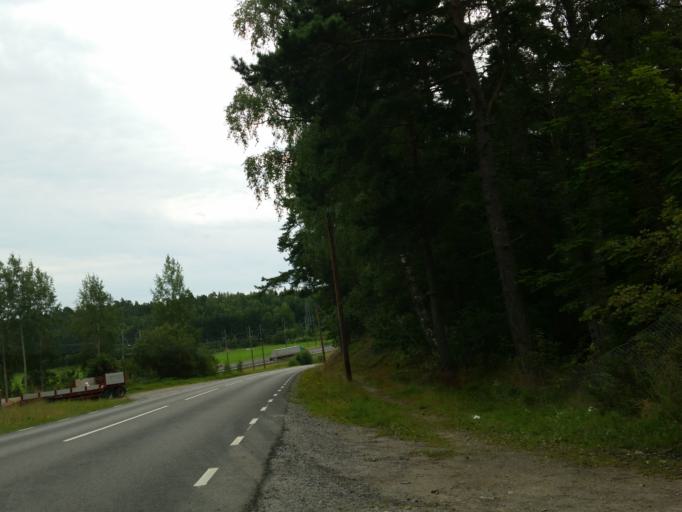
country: SE
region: Stockholm
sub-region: Botkyrka Kommun
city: Eriksberg
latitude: 59.2277
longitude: 17.7852
